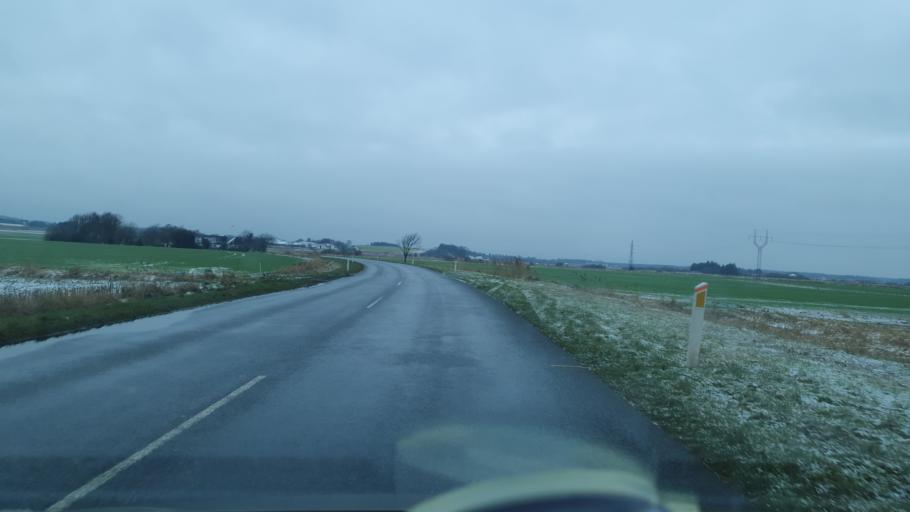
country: DK
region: North Denmark
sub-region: Jammerbugt Kommune
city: Brovst
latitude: 57.1158
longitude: 9.5002
